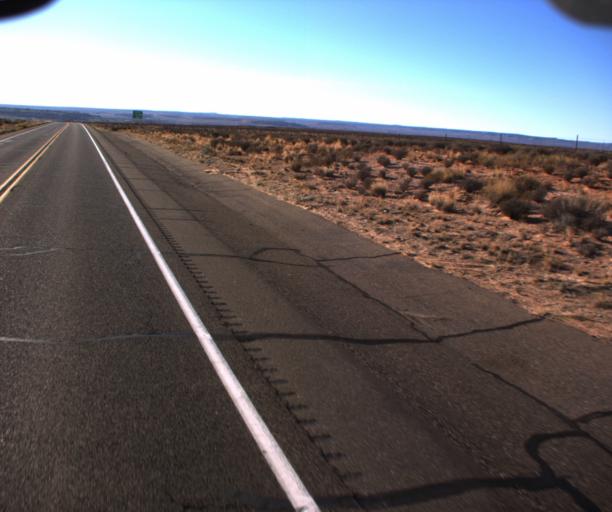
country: US
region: Arizona
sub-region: Coconino County
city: Page
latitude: 36.9640
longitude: -111.5099
